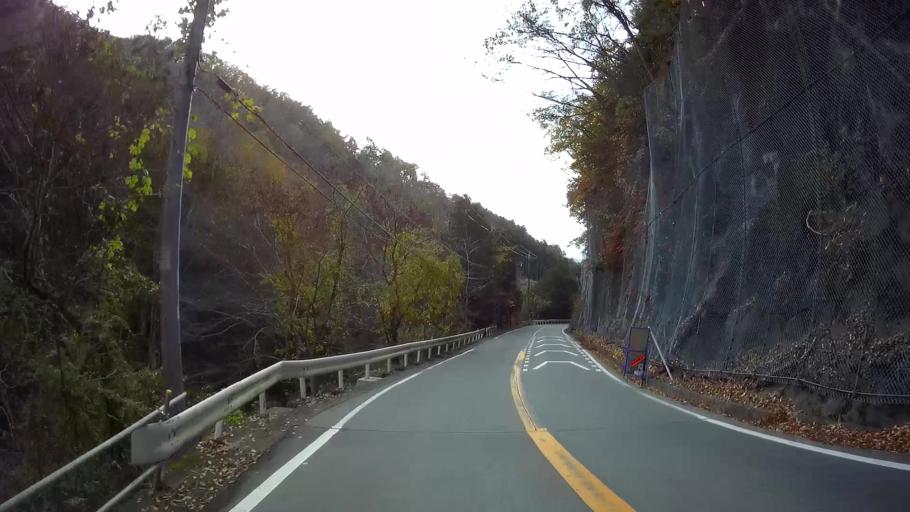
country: JP
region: Yamanashi
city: Fujikawaguchiko
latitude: 35.4741
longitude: 138.5432
